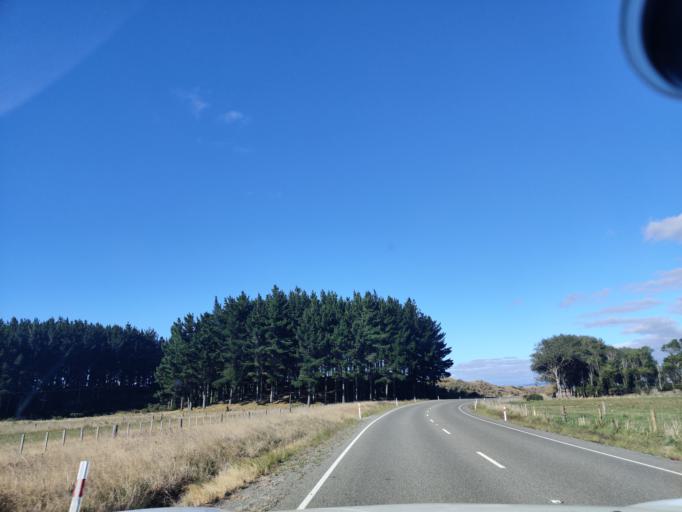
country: NZ
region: Manawatu-Wanganui
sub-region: Horowhenua District
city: Foxton
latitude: -40.4183
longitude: 175.4222
